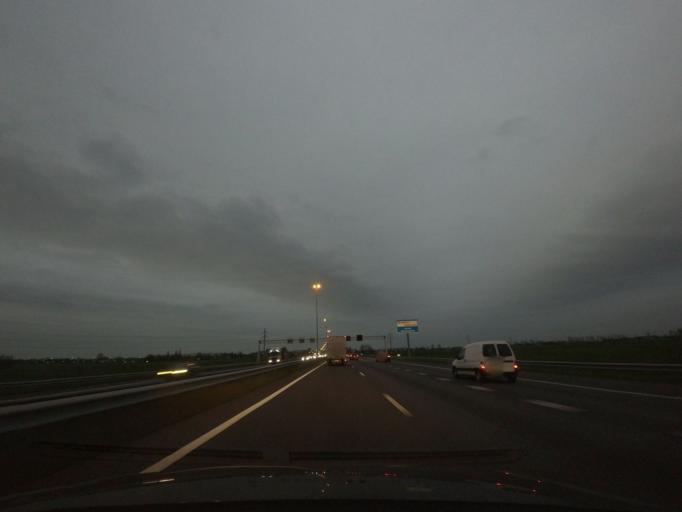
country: NL
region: South Holland
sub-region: Gemeente Gorinchem
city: Gorinchem
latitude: 51.8610
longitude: 4.9577
